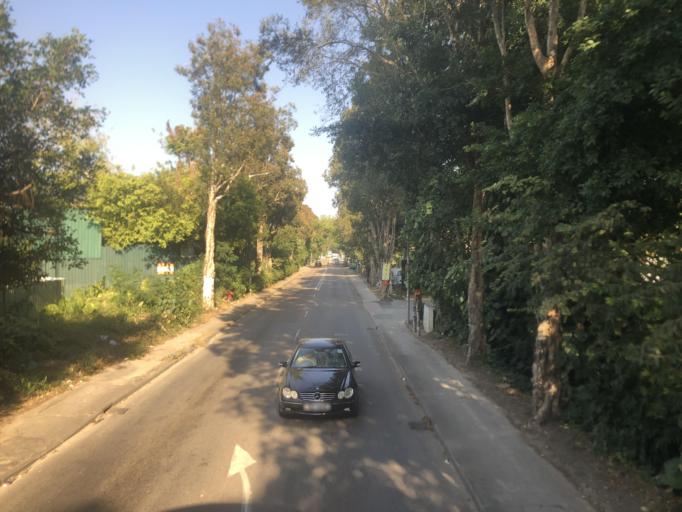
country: CN
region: Guangdong
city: Liantang
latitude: 22.5159
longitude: 114.1706
